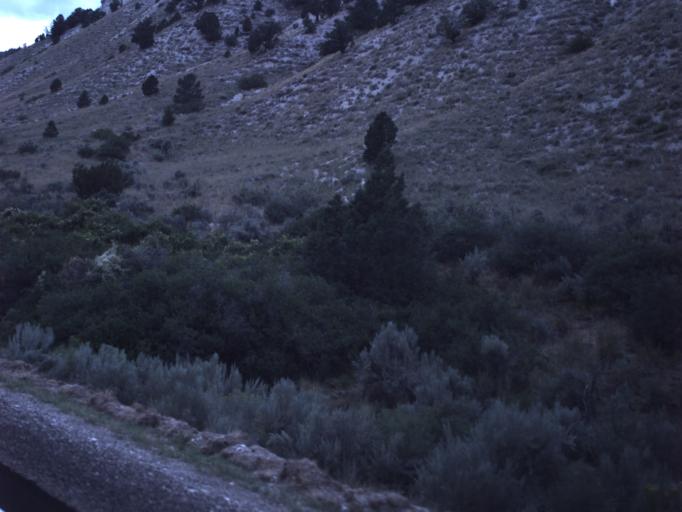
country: US
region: Utah
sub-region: Duchesne County
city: Duchesne
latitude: 39.9952
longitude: -110.5891
